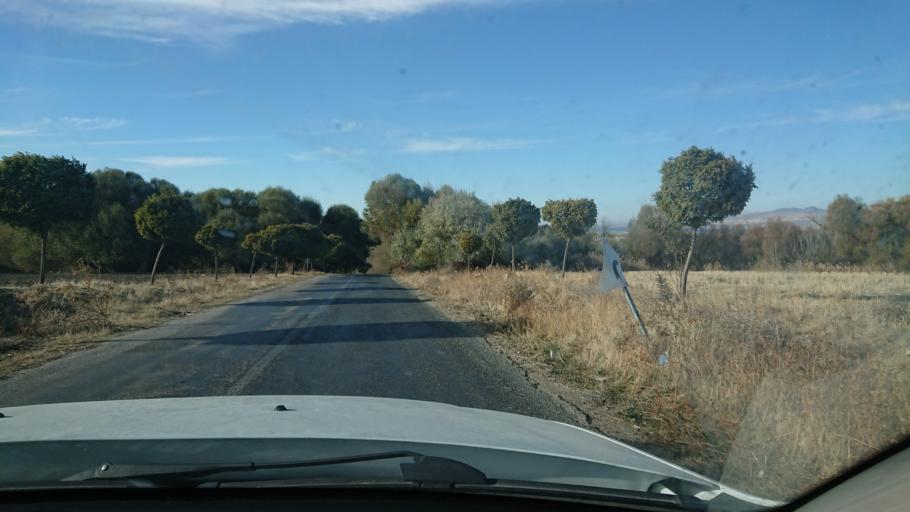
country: TR
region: Aksaray
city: Sariyahsi
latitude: 38.9696
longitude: 33.8677
